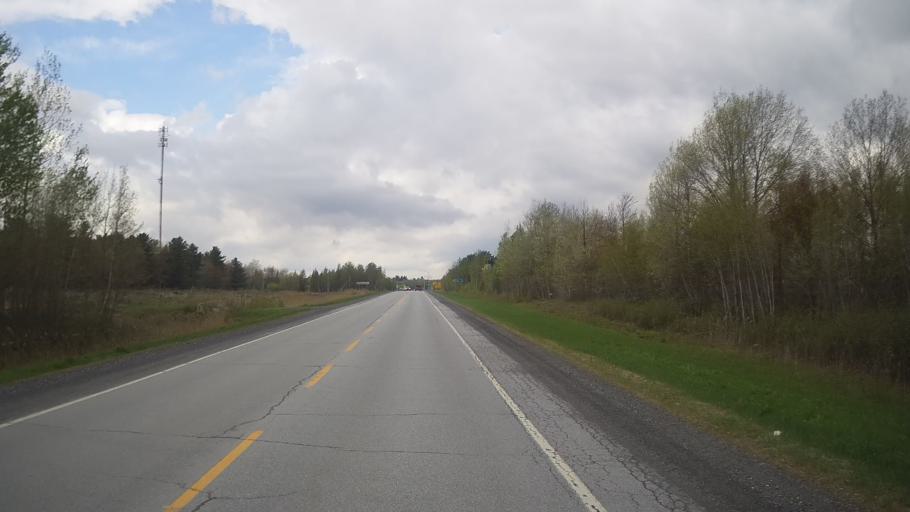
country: CA
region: Quebec
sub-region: Monteregie
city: Farnham
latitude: 45.2729
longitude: -72.9758
